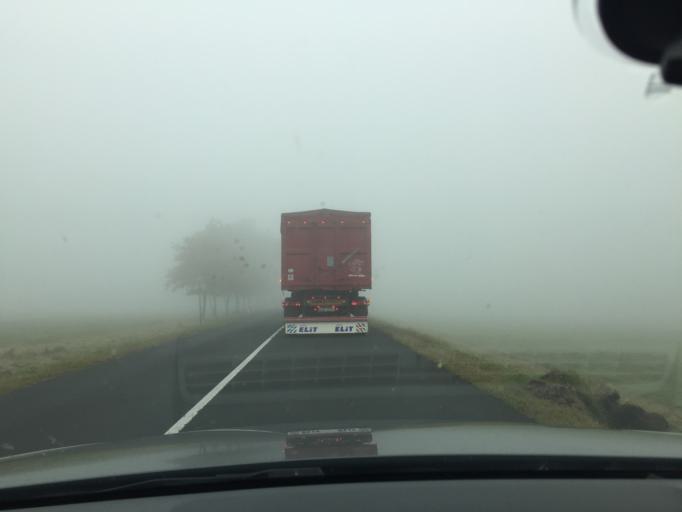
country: CZ
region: Ustecky
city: Libouchec
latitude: 50.7802
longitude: 13.9825
